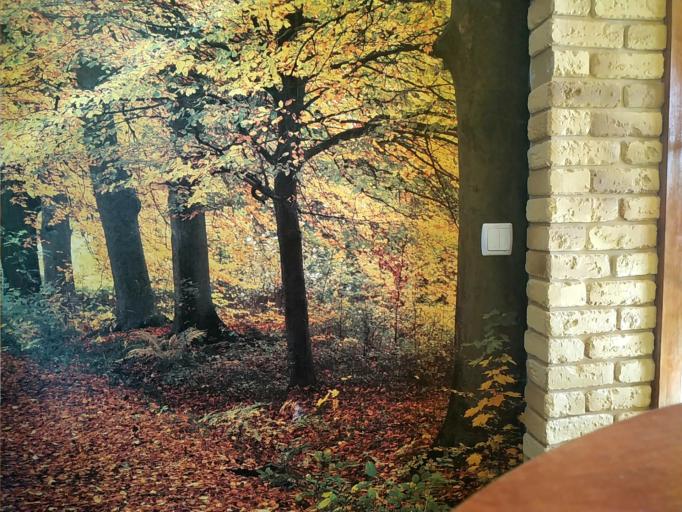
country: RU
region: Jaroslavl
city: Kukoboy
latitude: 58.8046
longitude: 39.7785
